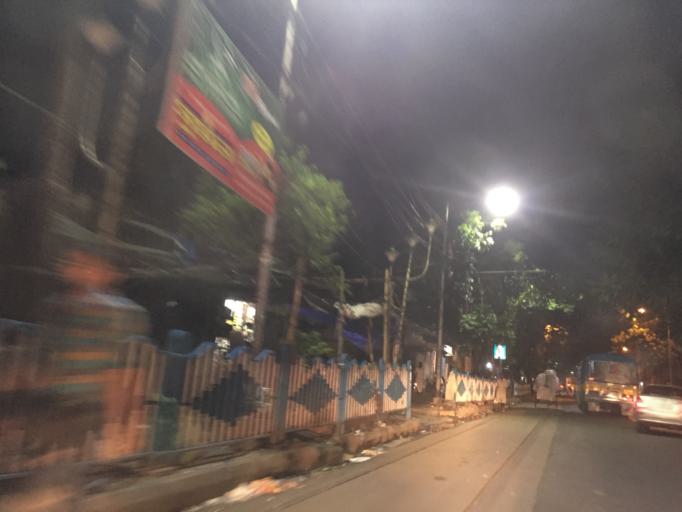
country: IN
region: West Bengal
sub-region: Kolkata
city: Bara Bazar
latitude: 22.5642
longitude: 88.3549
